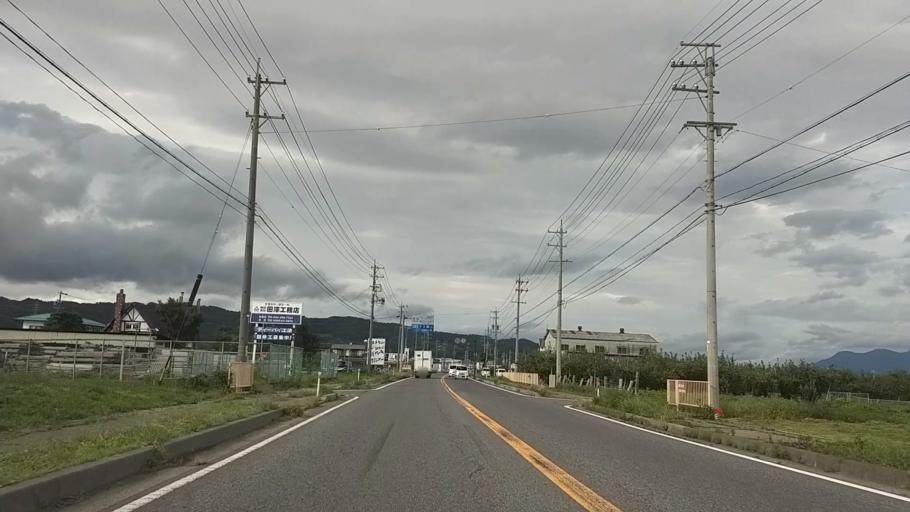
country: JP
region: Nagano
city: Suzaka
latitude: 36.6905
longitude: 138.2683
